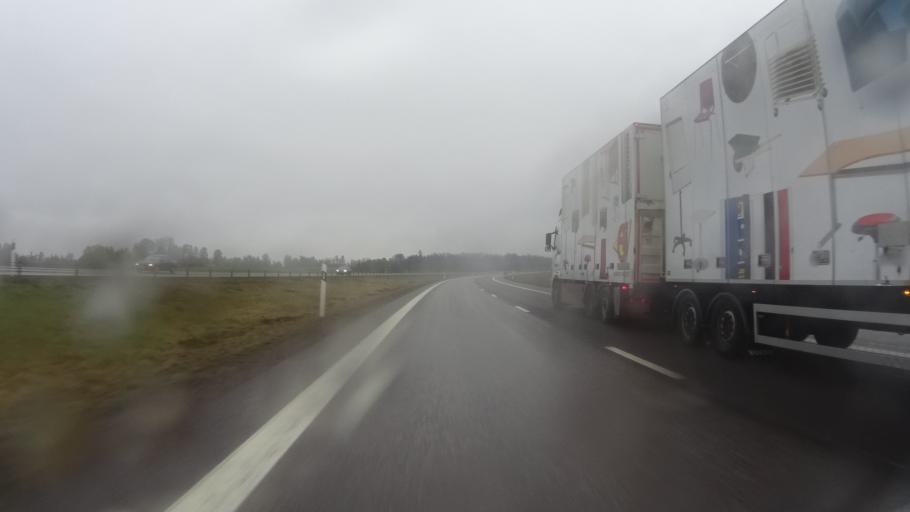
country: SE
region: Kronoberg
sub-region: Markaryds Kommun
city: Stromsnasbruk
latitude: 56.6515
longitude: 13.8047
